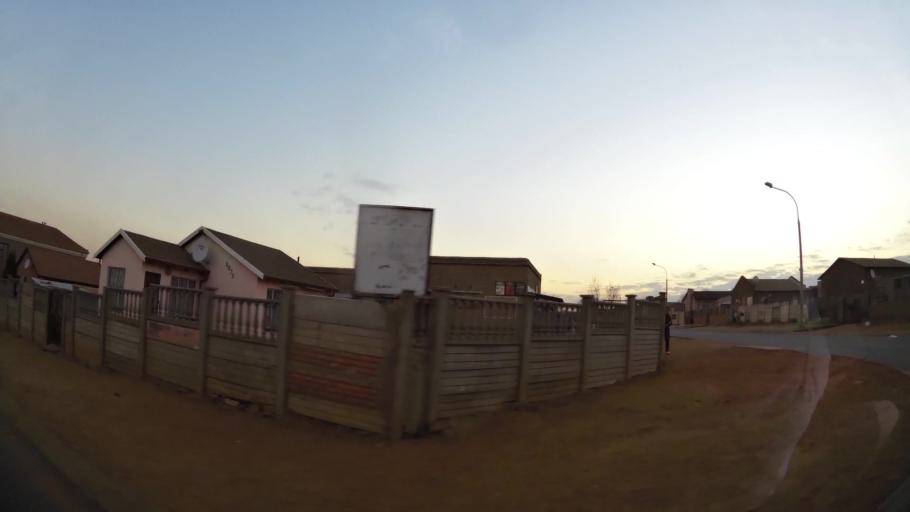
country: ZA
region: Gauteng
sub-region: West Rand District Municipality
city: Randfontein
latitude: -26.2094
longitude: 27.7136
